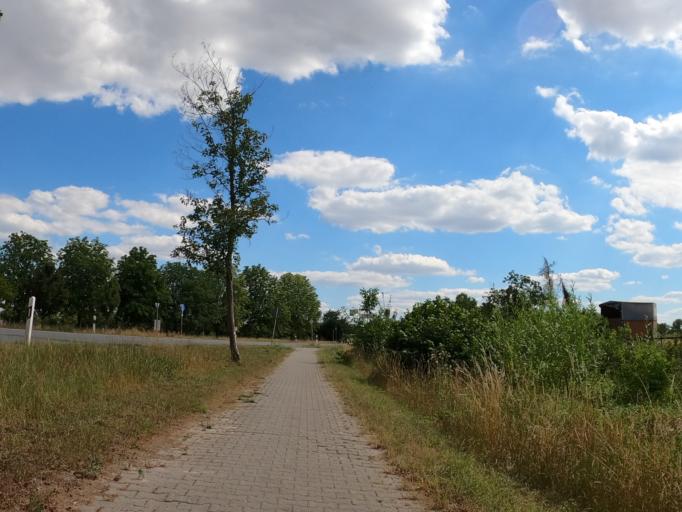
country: DE
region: Hesse
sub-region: Regierungsbezirk Darmstadt
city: Trebur
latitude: 49.9209
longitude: 8.4125
